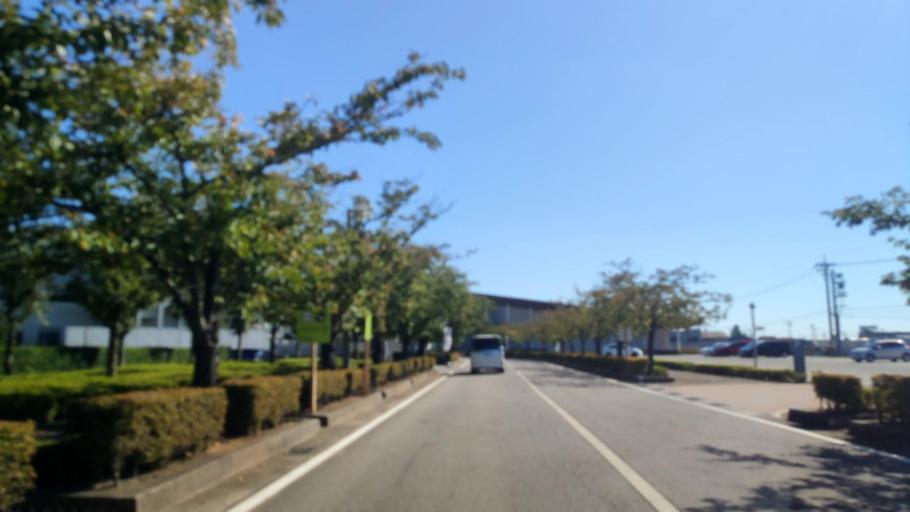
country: JP
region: Ishikawa
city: Nanao
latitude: 37.4441
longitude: 137.2696
